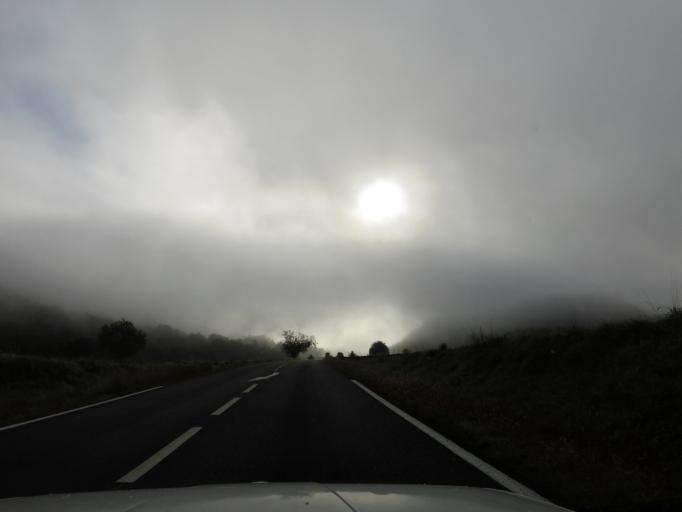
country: FR
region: Rhone-Alpes
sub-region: Departement de l'Isere
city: Creys-Mepieu
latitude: 45.7622
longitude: 5.4859
